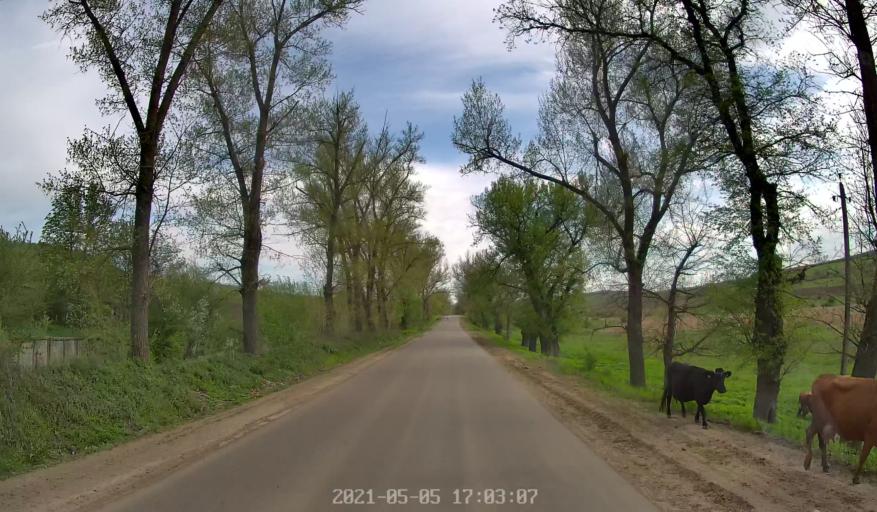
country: MD
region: Chisinau
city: Vadul lui Voda
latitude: 47.0540
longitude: 29.1329
